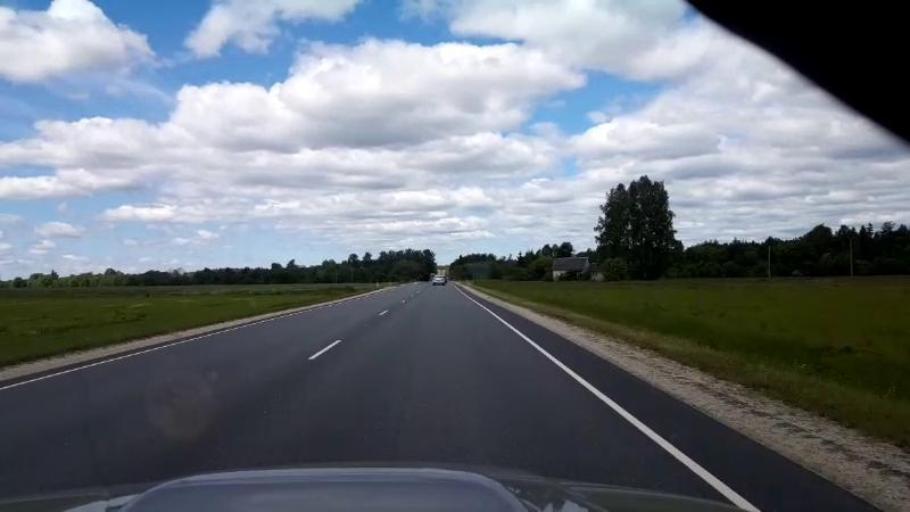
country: EE
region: Paernumaa
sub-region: Halinga vald
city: Parnu-Jaagupi
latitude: 58.6962
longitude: 24.4308
